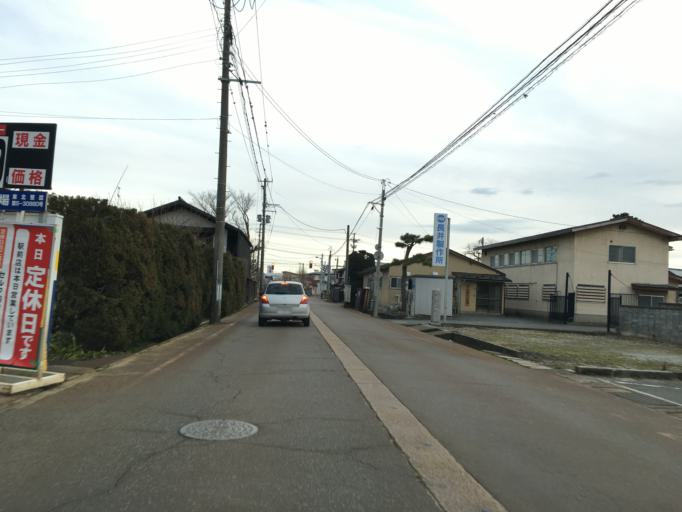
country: JP
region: Yamagata
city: Nagai
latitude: 38.1002
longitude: 140.0362
